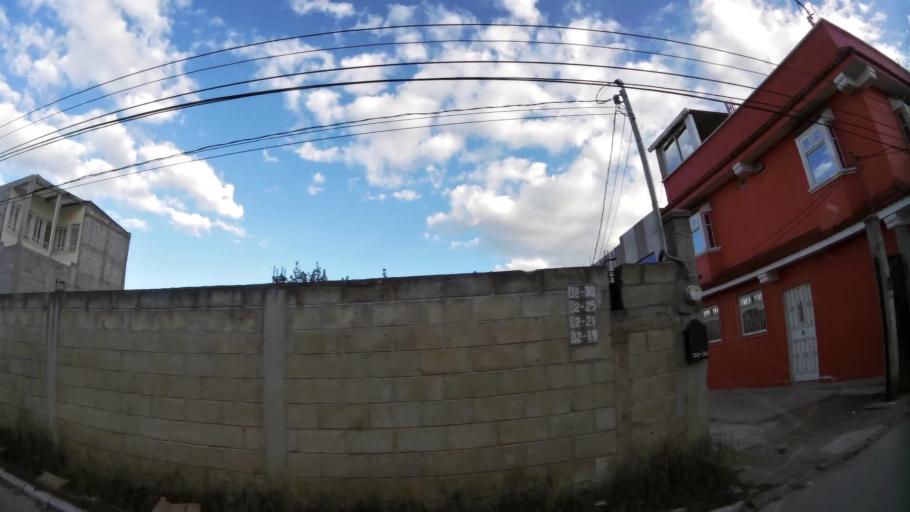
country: GT
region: Quetzaltenango
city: Quetzaltenango
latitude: 14.8524
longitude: -91.5316
